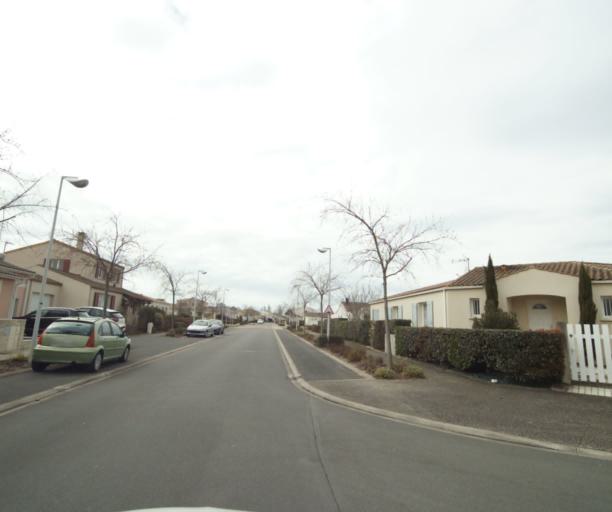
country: FR
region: Poitou-Charentes
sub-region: Departement de la Charente-Maritime
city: Lagord
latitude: 46.1858
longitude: -1.1619
